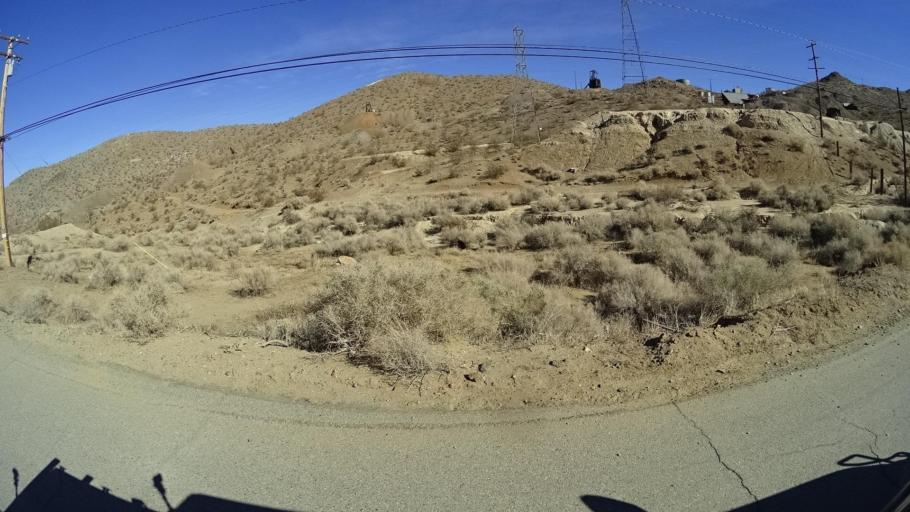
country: US
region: California
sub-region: Kern County
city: Ridgecrest
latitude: 35.3670
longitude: -117.6495
